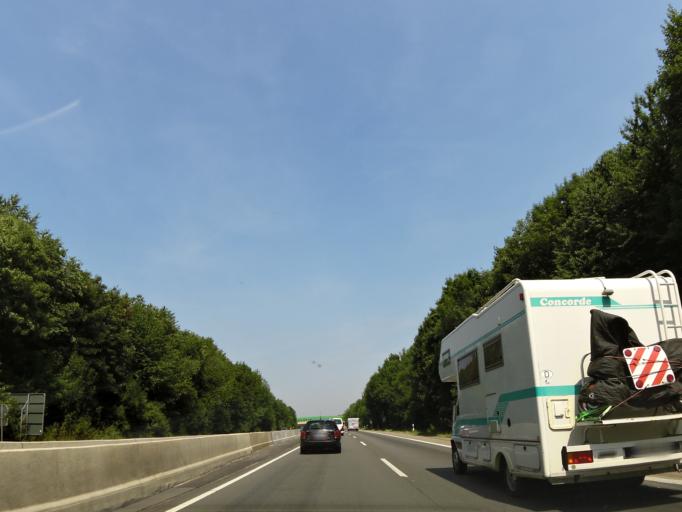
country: DE
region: North Rhine-Westphalia
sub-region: Regierungsbezirk Koln
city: Kerpen
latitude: 50.8857
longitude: 6.7024
